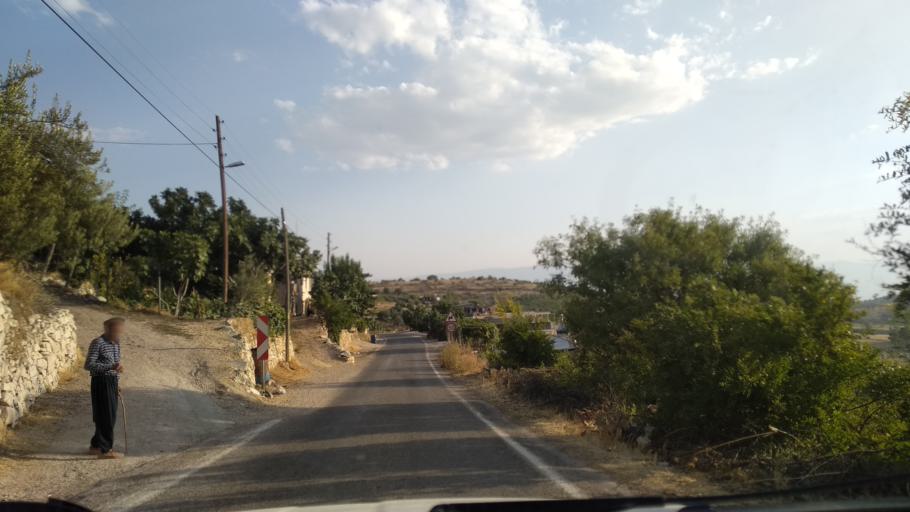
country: TR
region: Mersin
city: Sarikavak
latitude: 36.5792
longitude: 33.6441
